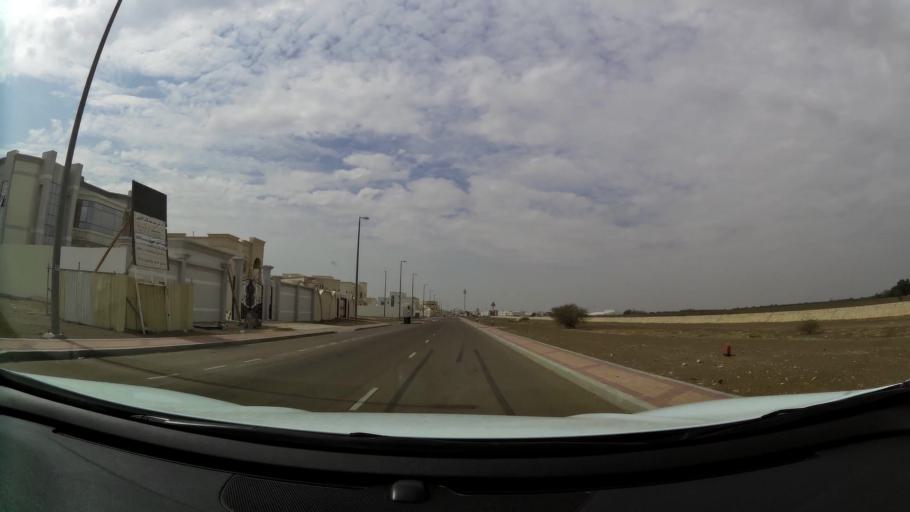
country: AE
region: Abu Dhabi
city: Al Ain
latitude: 24.1941
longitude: 55.8164
